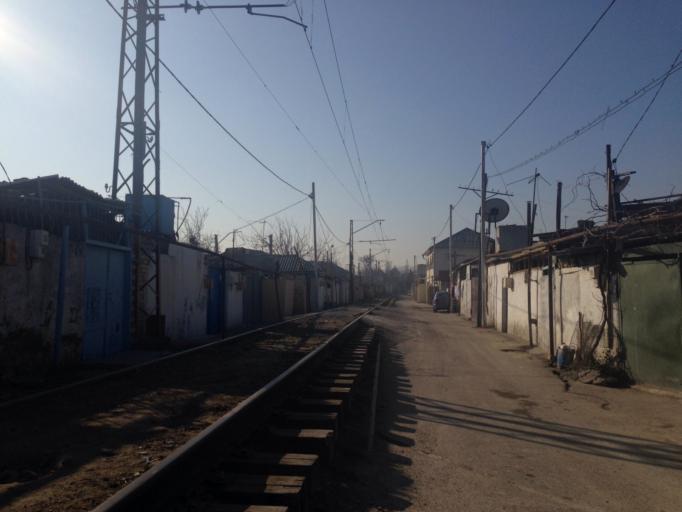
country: AZ
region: Baki
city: Baku
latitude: 40.3940
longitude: 49.8848
